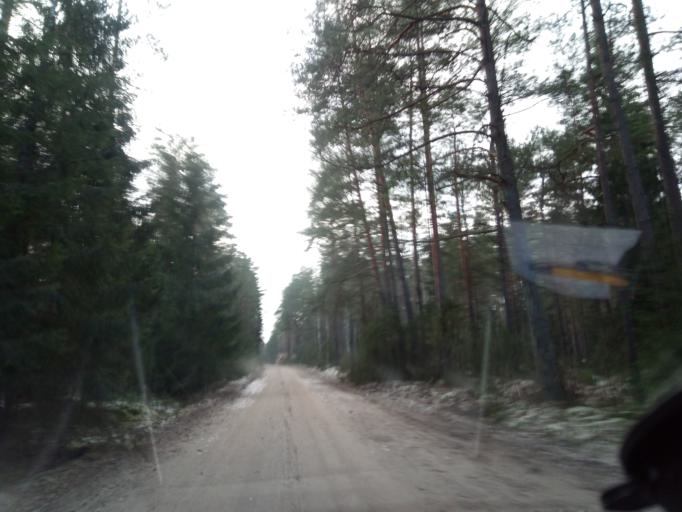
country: LT
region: Alytaus apskritis
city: Varena
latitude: 53.9725
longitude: 24.3247
